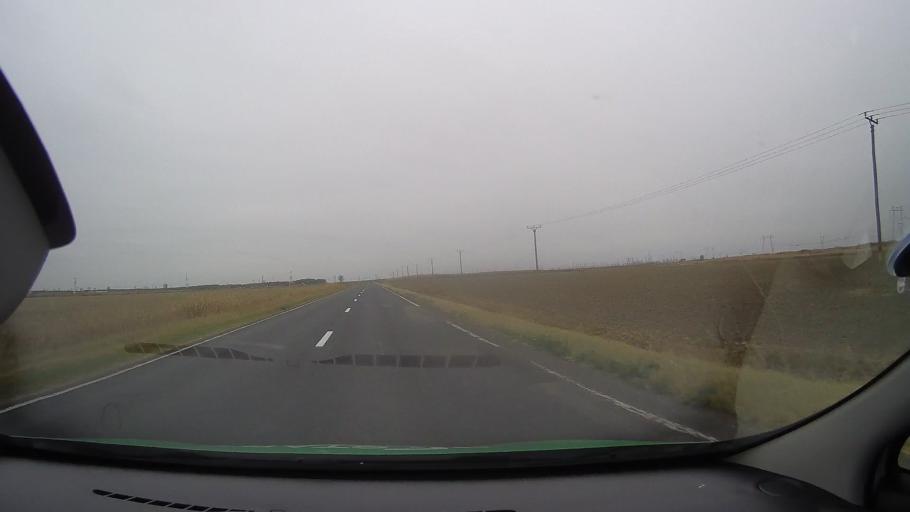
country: RO
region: Ialomita
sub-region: Comuna Gura Ialomitei
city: Gura Ialomitei
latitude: 44.6878
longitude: 27.7918
